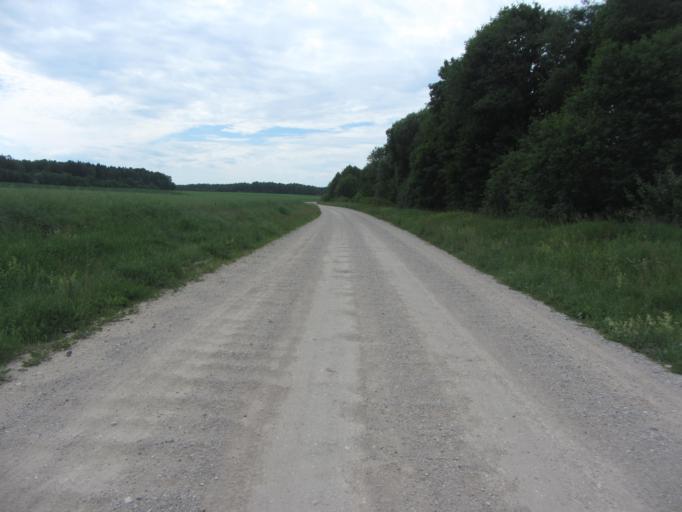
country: LT
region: Panevezys
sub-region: Birzai
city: Birzai
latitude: 56.4101
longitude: 24.8291
